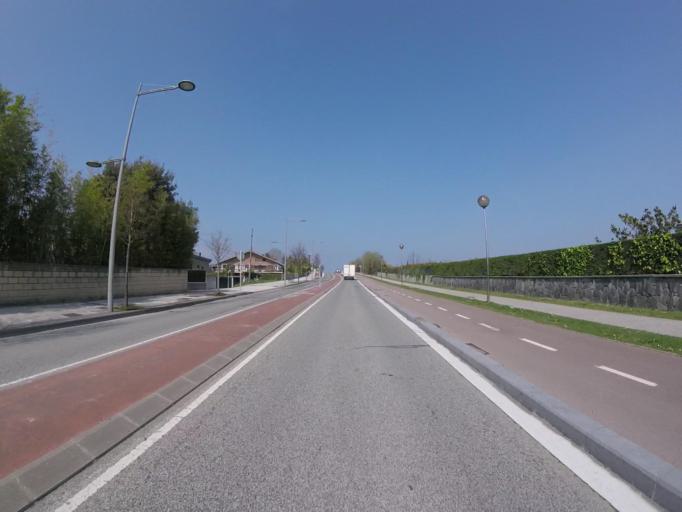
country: ES
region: Basque Country
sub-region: Provincia de Guipuzcoa
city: San Sebastian
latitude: 43.2924
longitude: -1.9910
